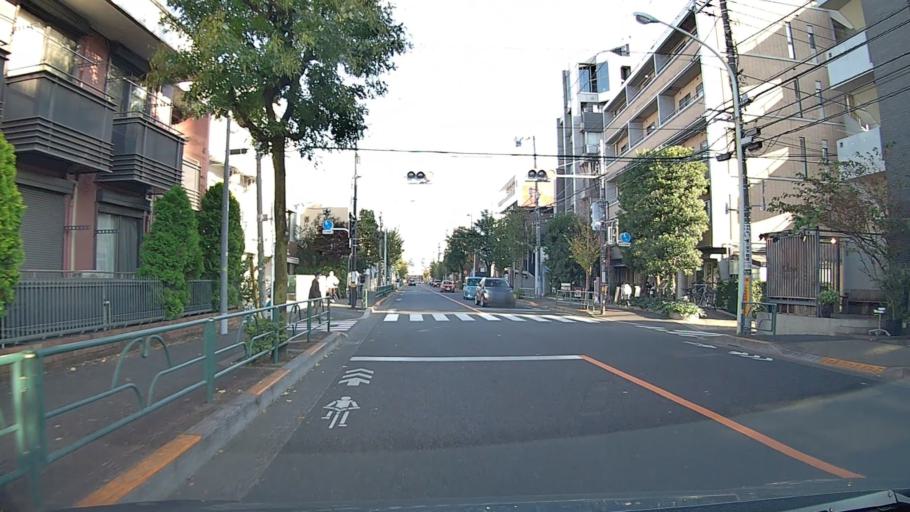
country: JP
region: Tokyo
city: Musashino
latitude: 35.7043
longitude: 139.5723
